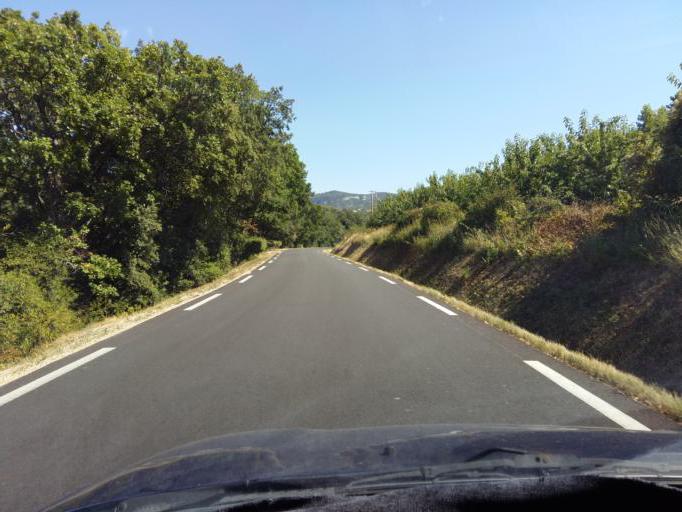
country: FR
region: Provence-Alpes-Cote d'Azur
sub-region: Departement du Vaucluse
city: Venasque
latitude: 44.0069
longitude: 5.1391
